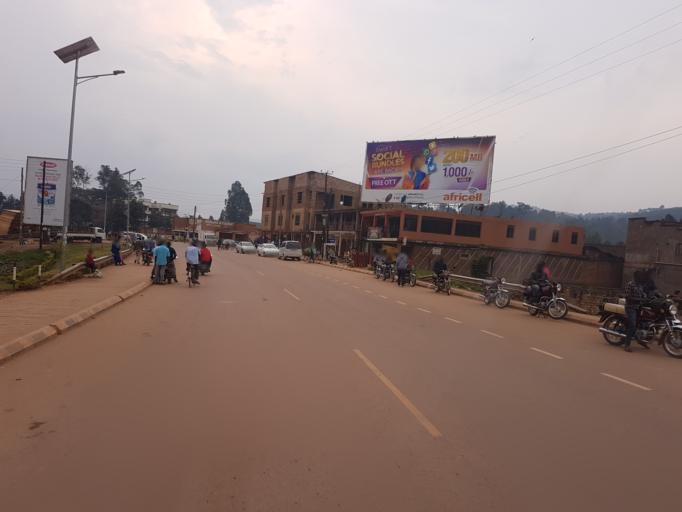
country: UG
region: Western Region
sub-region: Kabale District
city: Kabale
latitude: -1.2487
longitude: 29.9850
